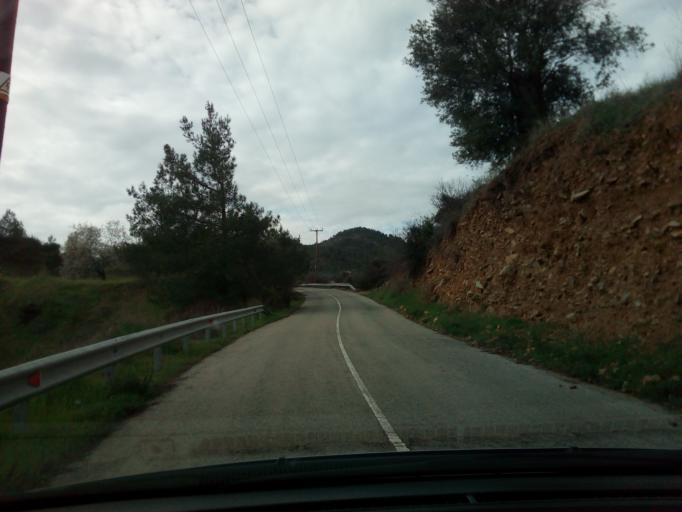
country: CY
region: Lefkosia
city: Klirou
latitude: 34.9769
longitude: 33.1815
